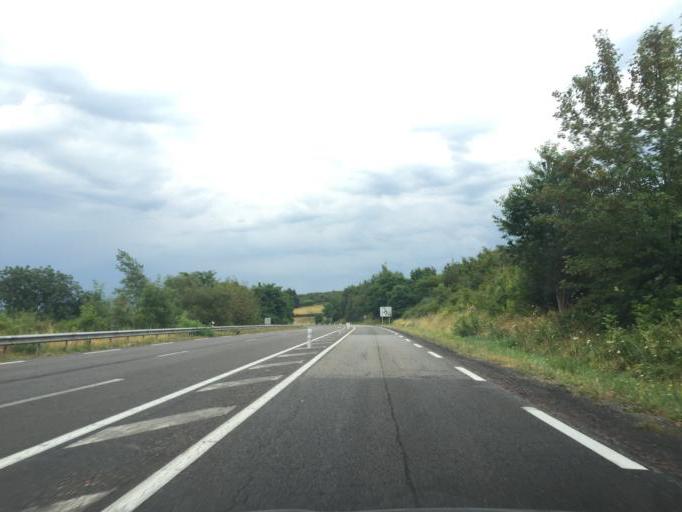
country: FR
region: Rhone-Alpes
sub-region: Departement de la Loire
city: La Pacaudiere
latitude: 46.2064
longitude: 3.8111
